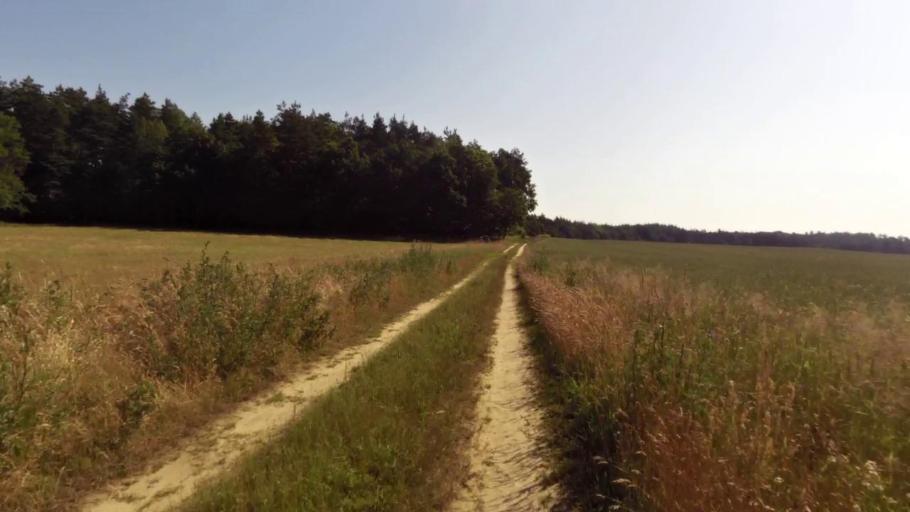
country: PL
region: West Pomeranian Voivodeship
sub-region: Powiat swidwinski
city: Polczyn-Zdroj
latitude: 53.8956
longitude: 16.0800
